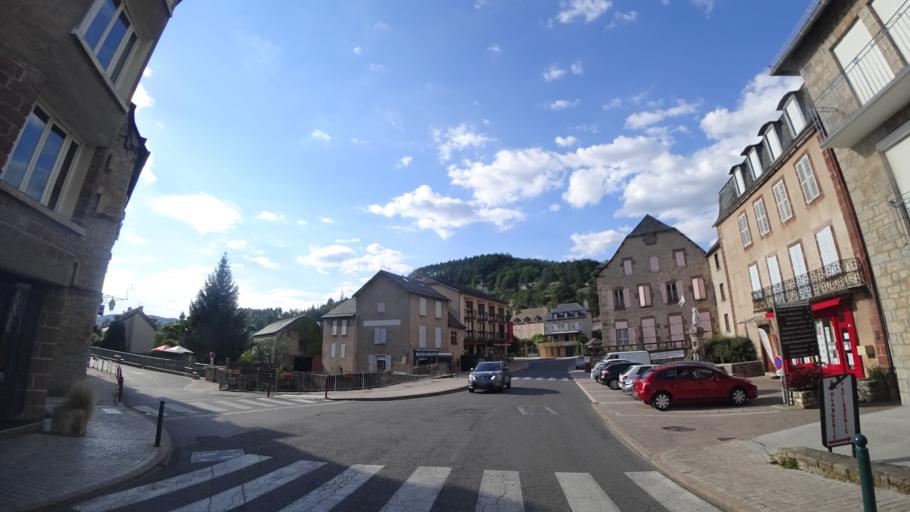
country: FR
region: Languedoc-Roussillon
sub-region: Departement de la Lozere
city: La Canourgue
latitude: 44.4325
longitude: 3.2144
